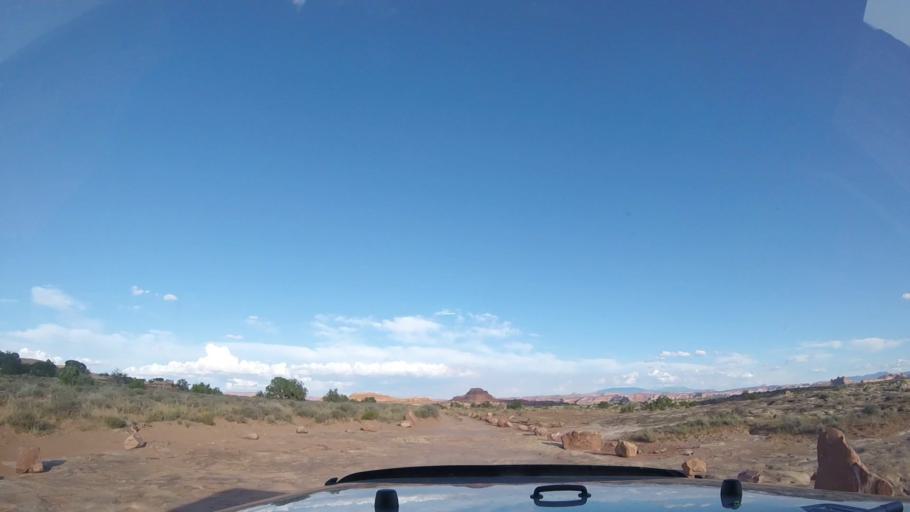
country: US
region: Utah
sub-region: Grand County
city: Moab
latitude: 38.1995
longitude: -109.7821
